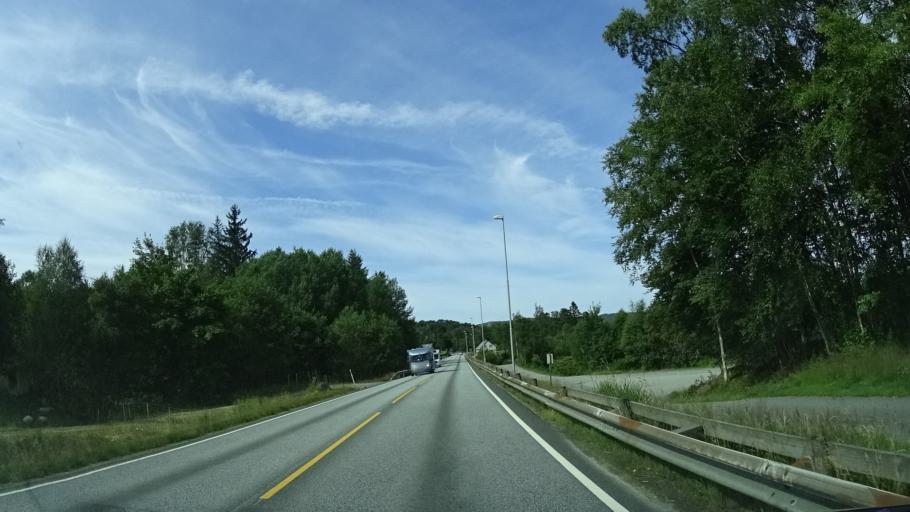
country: NO
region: Hordaland
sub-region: Bomlo
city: Mosterhamn
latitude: 59.6085
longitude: 5.4731
